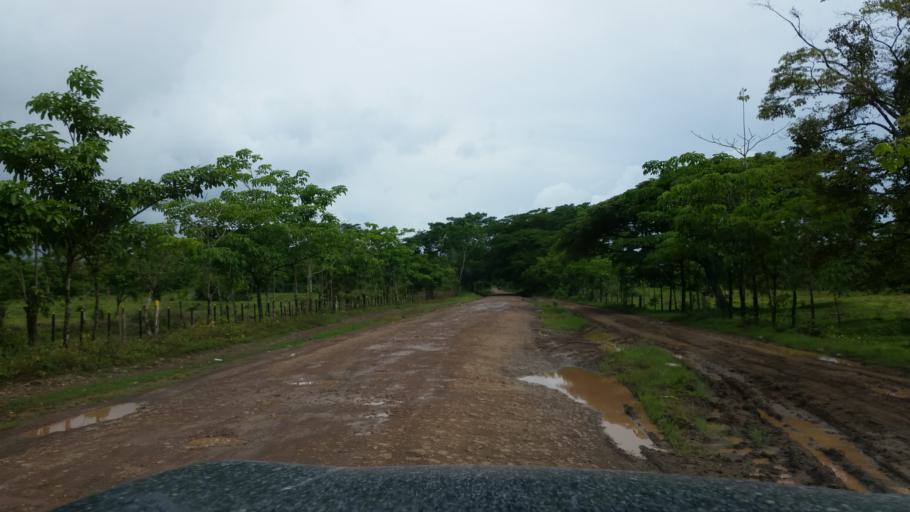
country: NI
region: Atlantico Norte (RAAN)
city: Siuna
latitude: 13.4281
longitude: -84.8525
